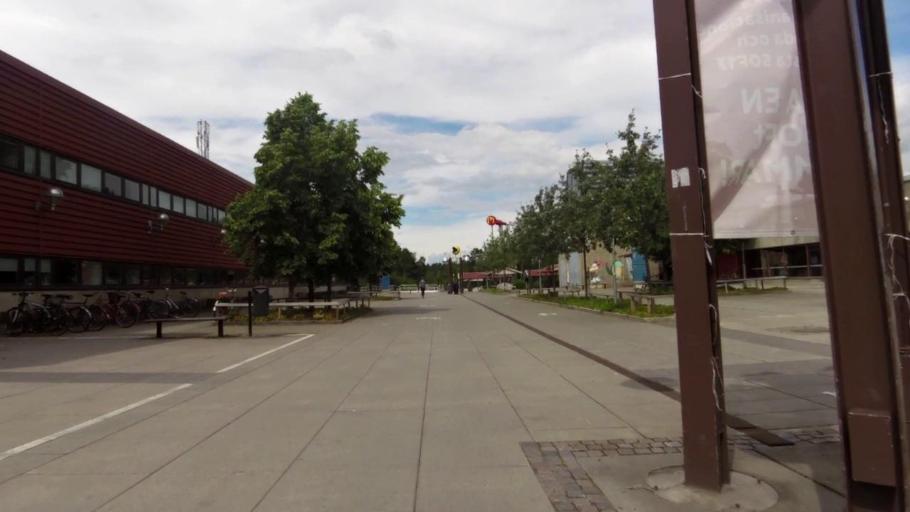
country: SE
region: OEstergoetland
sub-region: Linkopings Kommun
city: Linkoping
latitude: 58.4023
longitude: 15.5778
